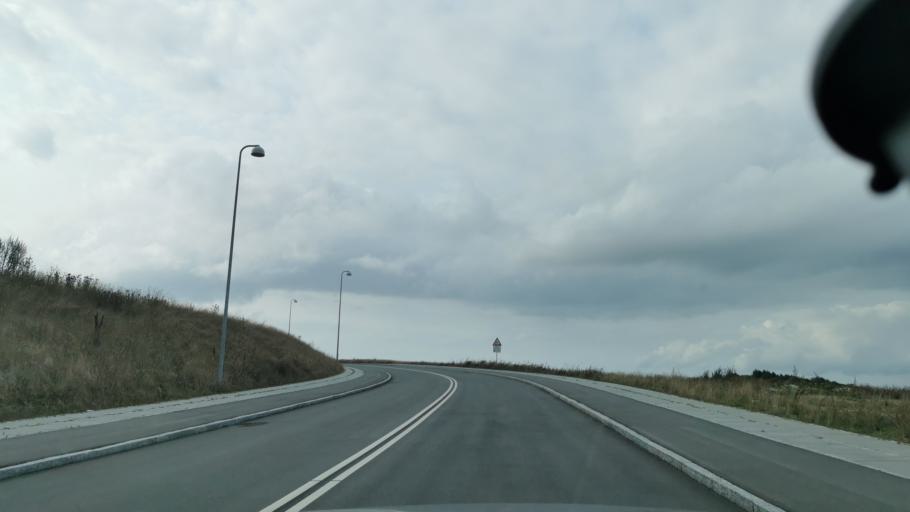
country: DK
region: Zealand
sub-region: Kalundborg Kommune
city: Kalundborg
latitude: 55.6938
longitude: 11.0822
